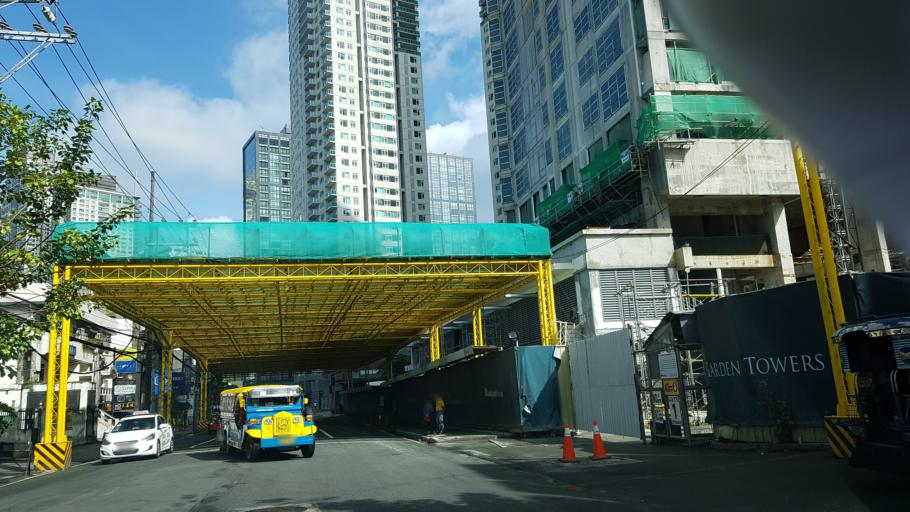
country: PH
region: Metro Manila
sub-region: Makati City
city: Makati City
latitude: 14.5488
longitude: 121.0250
